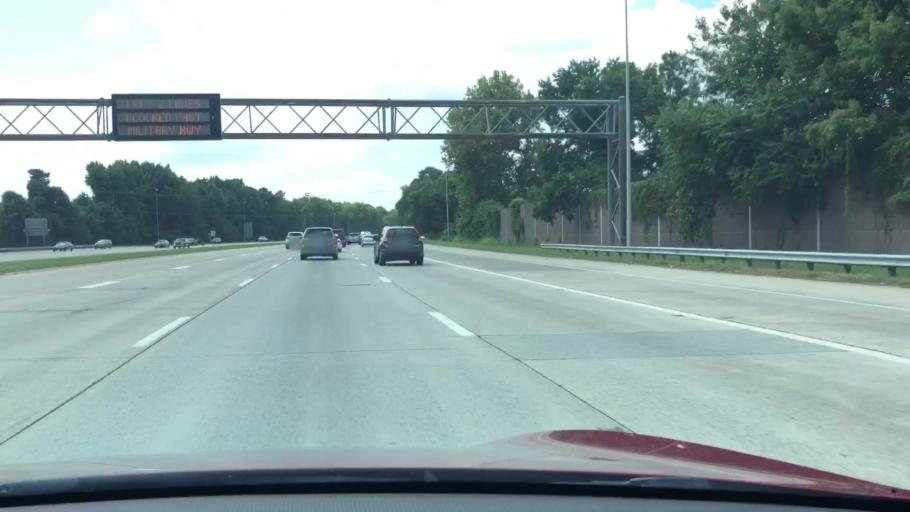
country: US
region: Virginia
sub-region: City of Chesapeake
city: Chesapeake
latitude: 36.8046
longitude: -76.1973
